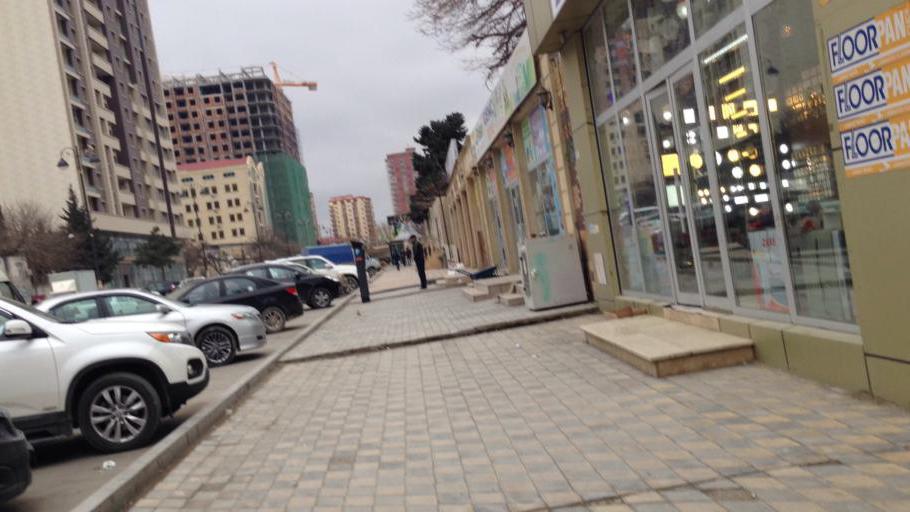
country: AZ
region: Baki
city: Baku
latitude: 40.3967
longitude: 49.8437
